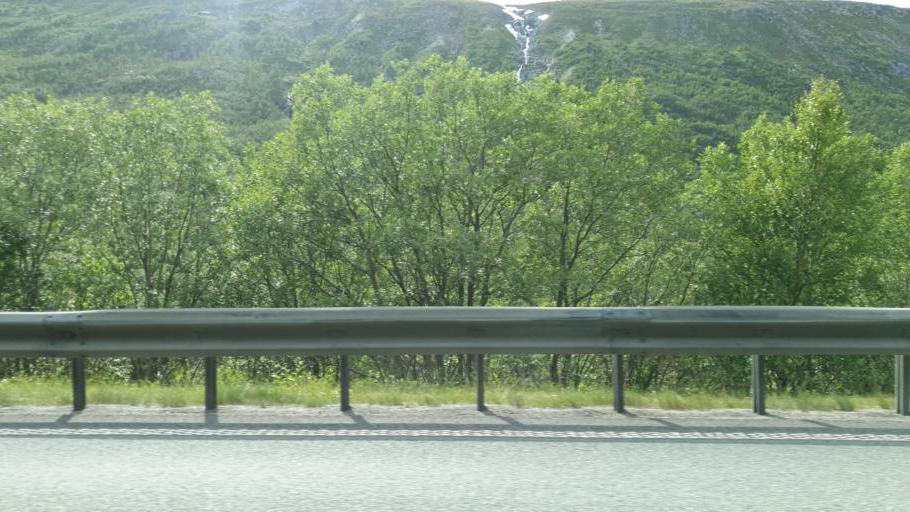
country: NO
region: Sor-Trondelag
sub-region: Oppdal
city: Oppdal
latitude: 62.4115
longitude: 9.6374
